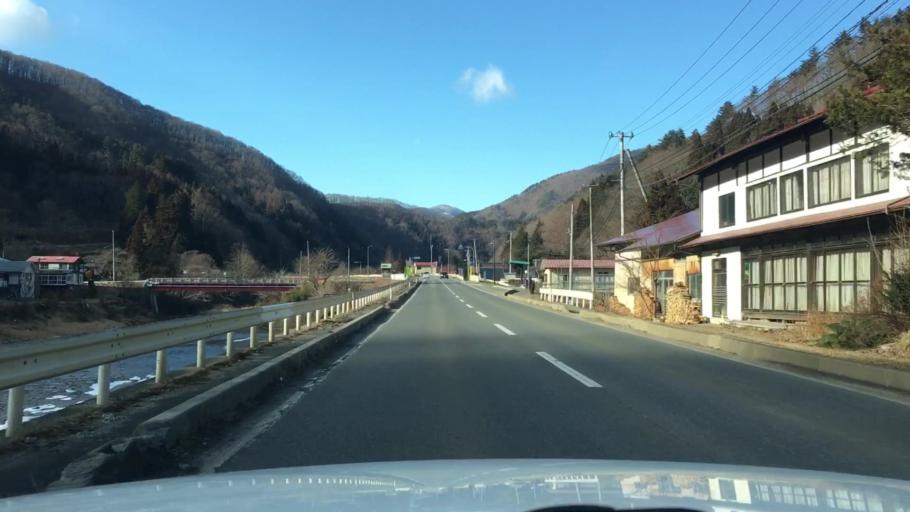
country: JP
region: Iwate
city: Tono
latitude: 39.6131
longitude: 141.6292
